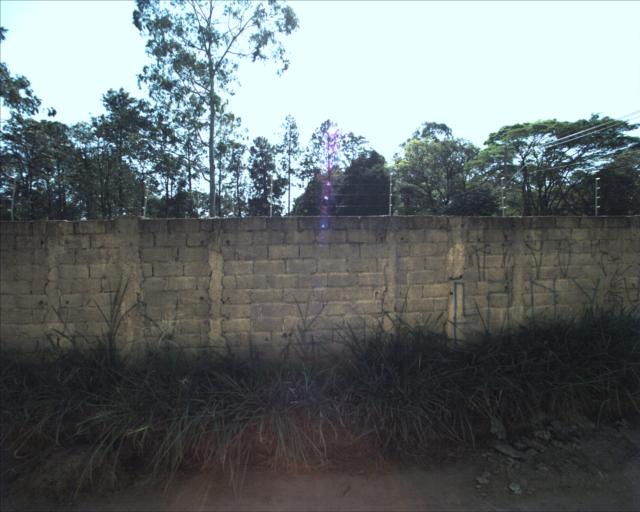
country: BR
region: Sao Paulo
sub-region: Aracoiaba Da Serra
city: Aracoiaba da Serra
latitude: -23.4826
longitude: -47.5380
